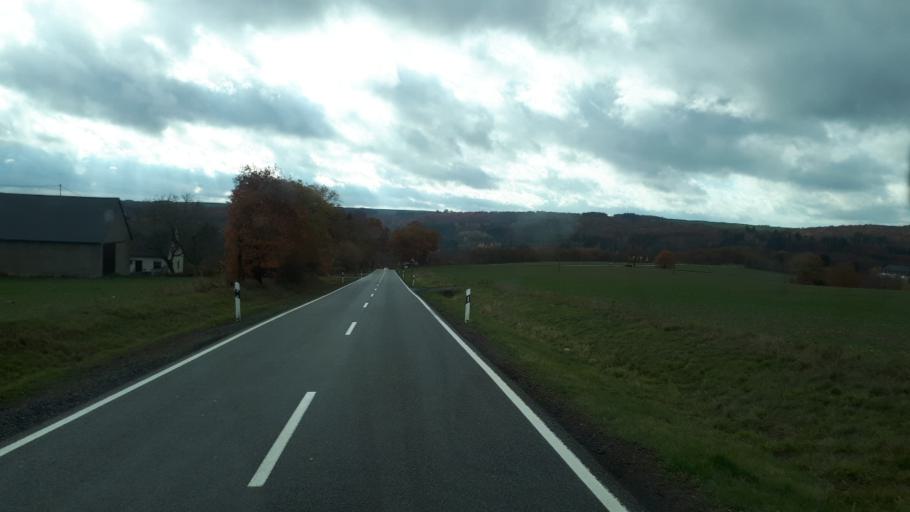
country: DE
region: Rheinland-Pfalz
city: Leienkaul
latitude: 50.2082
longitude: 7.0991
